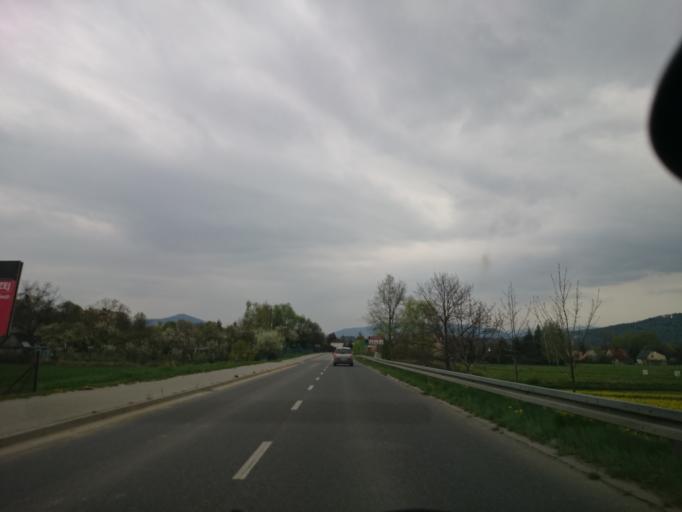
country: PL
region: Opole Voivodeship
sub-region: Powiat nyski
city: Glucholazy
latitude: 50.3287
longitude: 17.3903
